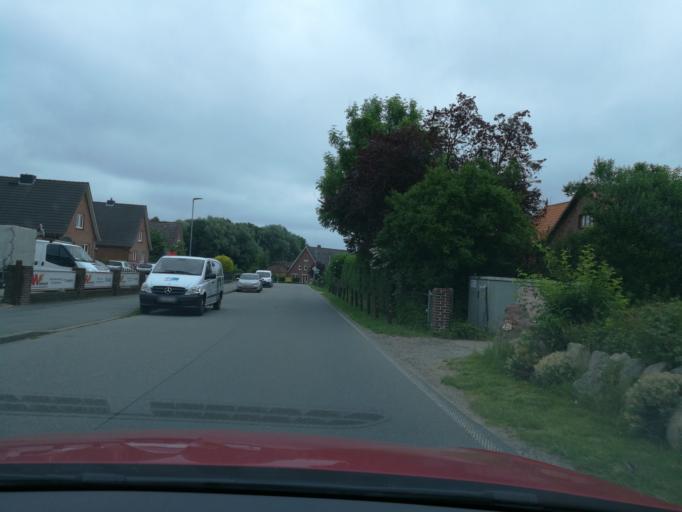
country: DE
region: Schleswig-Holstein
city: Lasbek
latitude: 53.7458
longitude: 10.3780
